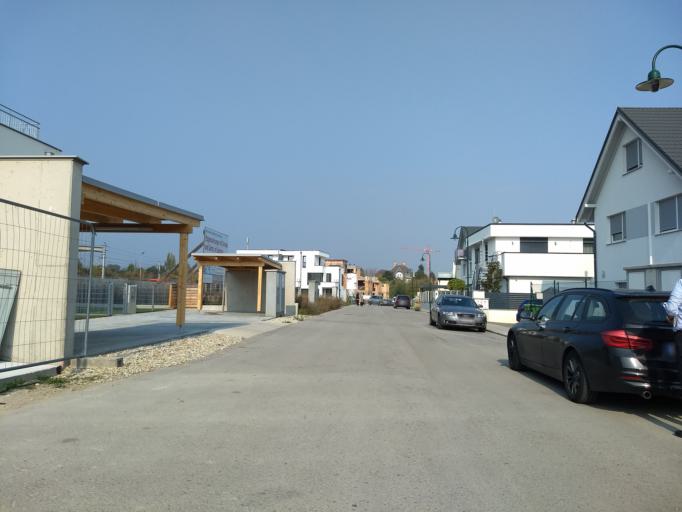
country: AT
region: Lower Austria
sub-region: Politischer Bezirk Modling
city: Brunn am Gebirge
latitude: 48.1276
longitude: 16.2857
